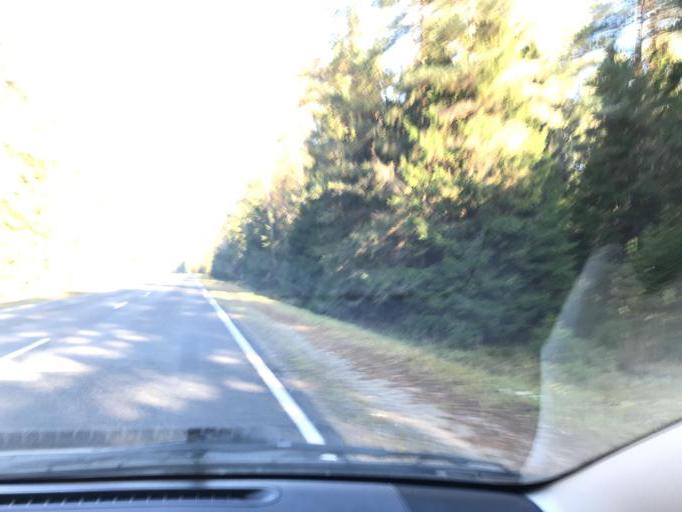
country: BY
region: Vitebsk
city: Lyepyel'
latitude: 54.9672
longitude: 28.7450
